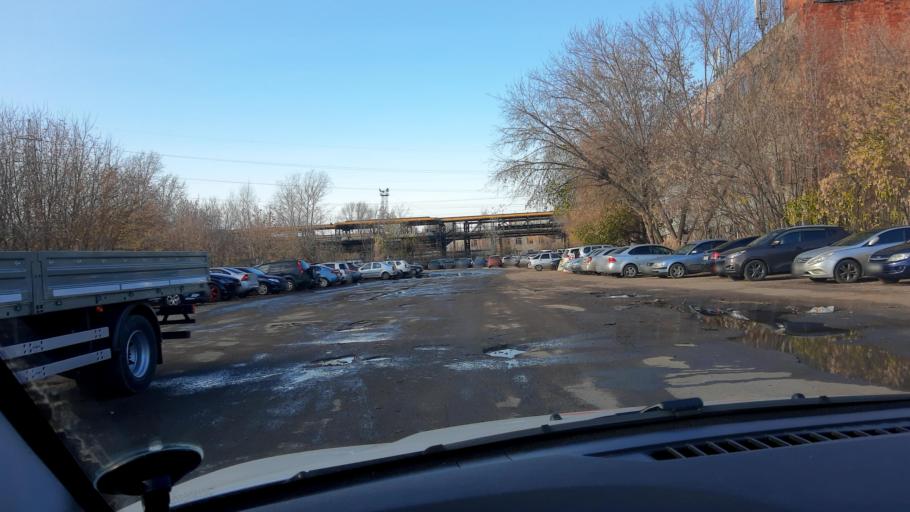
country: RU
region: Nizjnij Novgorod
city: Nizhniy Novgorod
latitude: 56.2413
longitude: 43.9060
